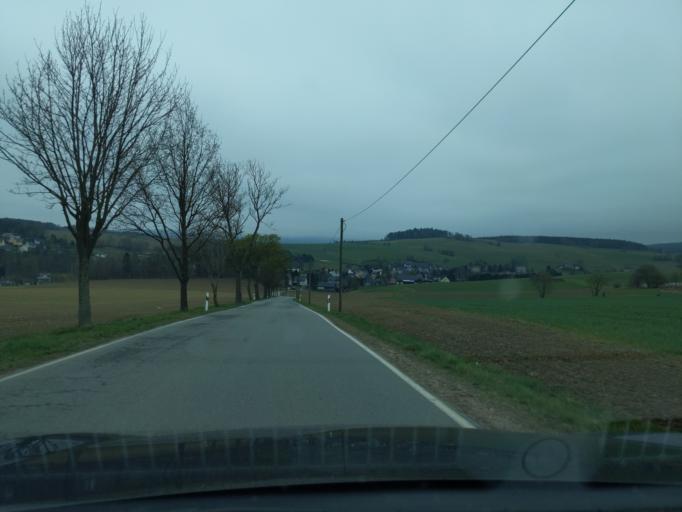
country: DE
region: Saxony
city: Zschorlau
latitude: 50.5771
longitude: 12.6494
